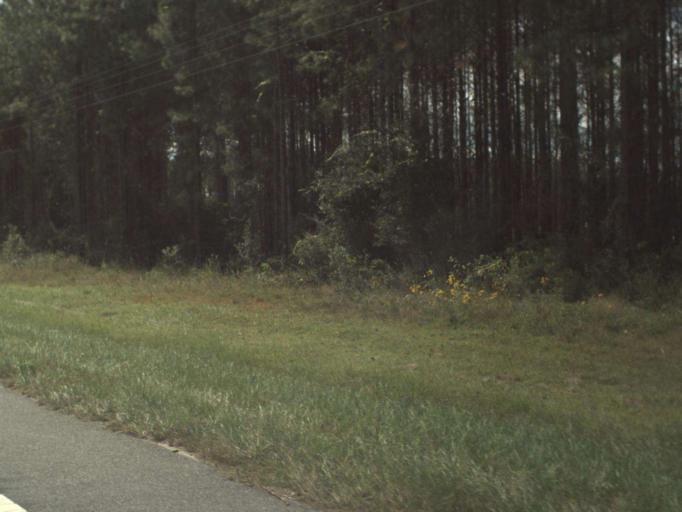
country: US
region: Florida
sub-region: Gulf County
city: Wewahitchka
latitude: 30.2994
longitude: -85.2375
